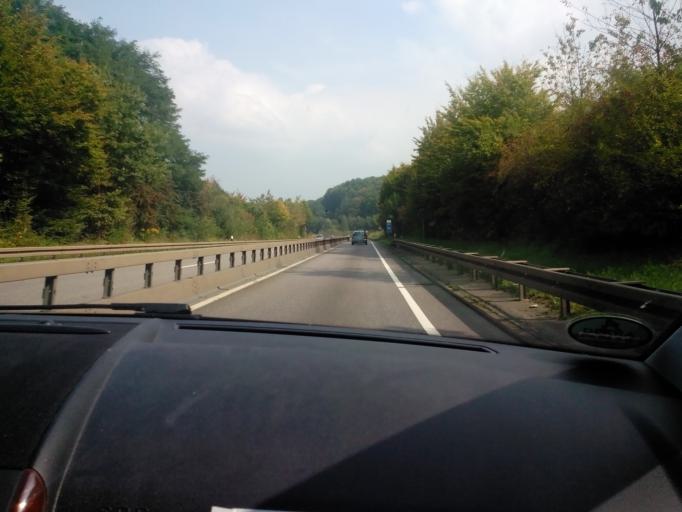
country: DE
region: Saarland
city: Mettlach
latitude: 49.4535
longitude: 6.5572
